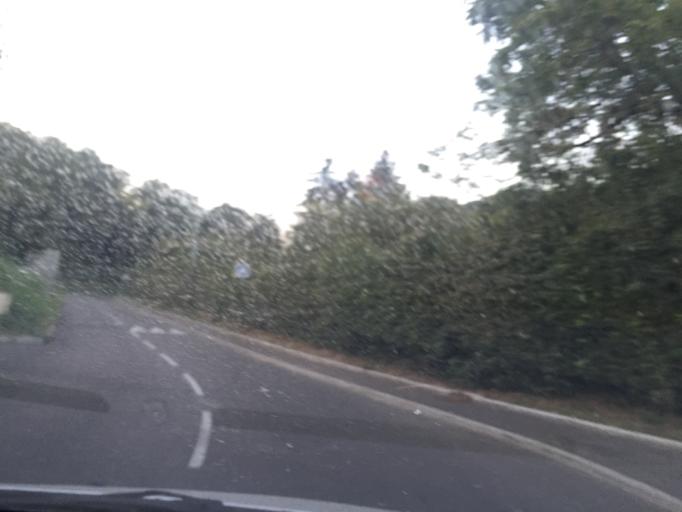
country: FR
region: Rhone-Alpes
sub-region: Departement de l'Ain
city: Saint-Maurice-de-Beynost
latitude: 45.8363
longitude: 4.9760
